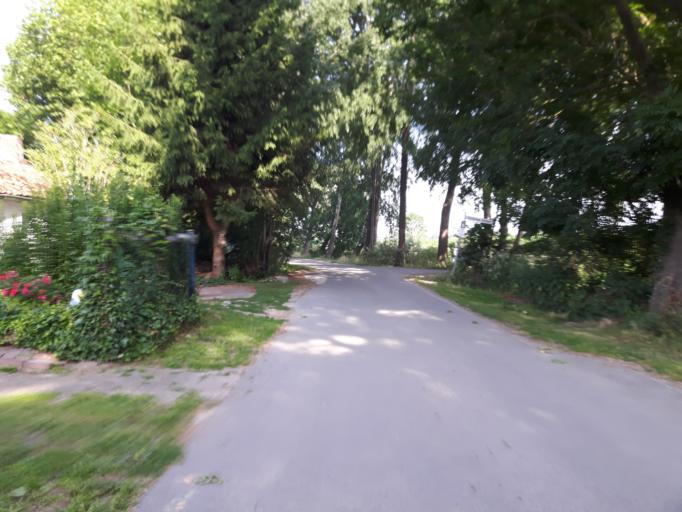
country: DE
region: Lower Saxony
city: Lemwerder
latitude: 53.1487
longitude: 8.5596
